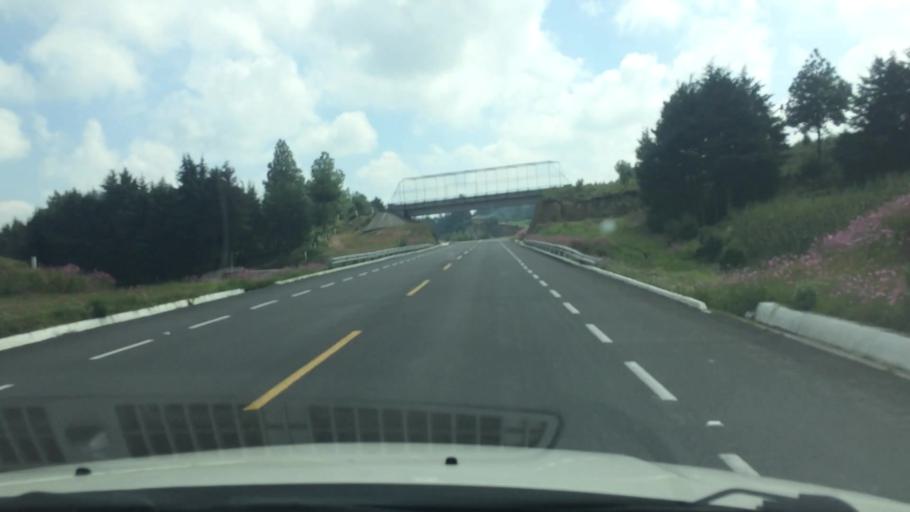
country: MX
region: Mexico
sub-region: Villa Victoria
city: Colonia Doctor Gustavo Baz
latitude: 19.3572
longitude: -99.9617
